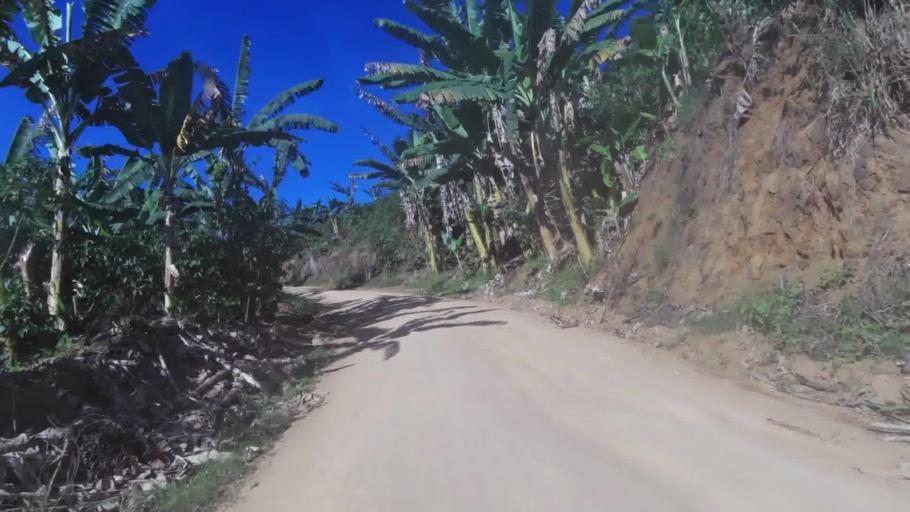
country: BR
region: Espirito Santo
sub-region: Iconha
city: Iconha
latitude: -20.7564
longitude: -40.8150
